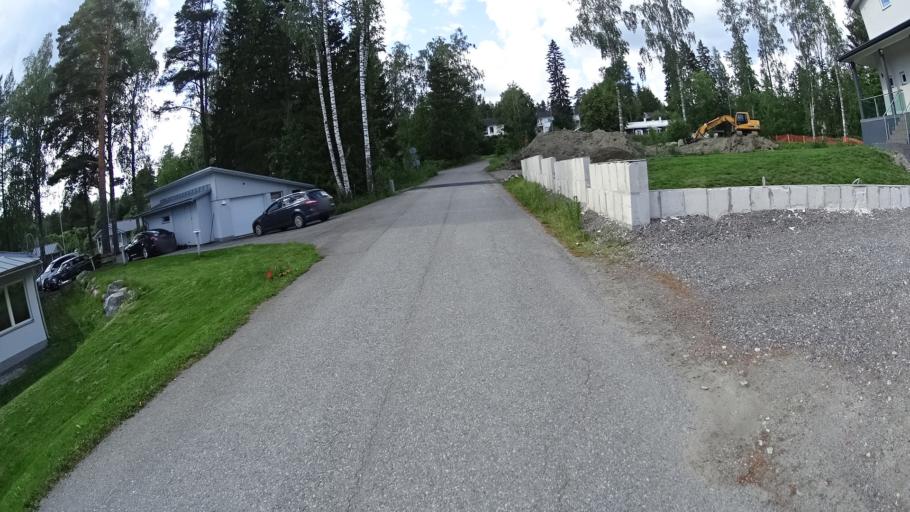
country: FI
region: Uusimaa
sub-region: Helsinki
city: Sibbo
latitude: 60.2609
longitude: 25.2319
